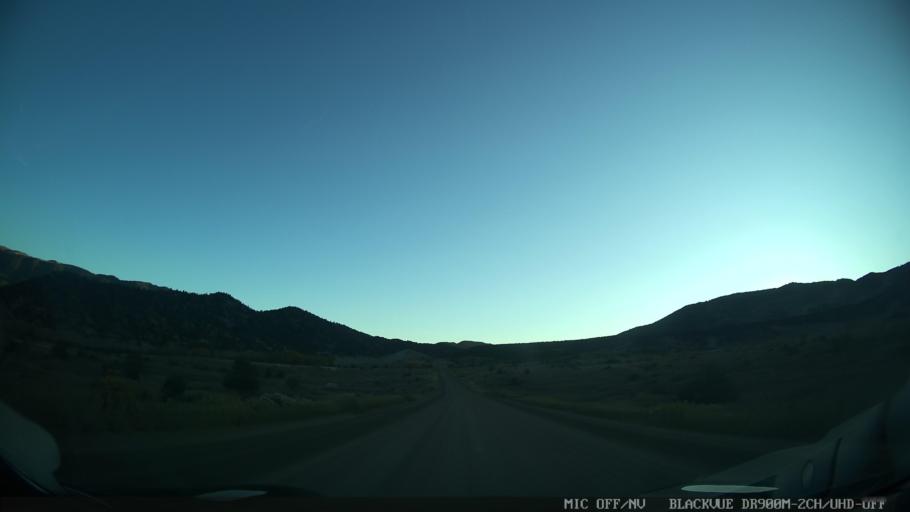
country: US
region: Colorado
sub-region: Eagle County
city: Edwards
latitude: 39.8999
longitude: -106.5949
